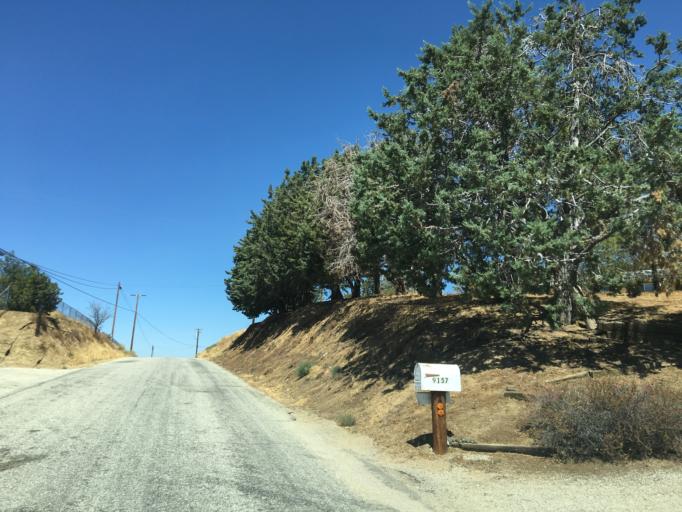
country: US
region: California
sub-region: Los Angeles County
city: Leona Valley
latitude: 34.6240
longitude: -118.2924
